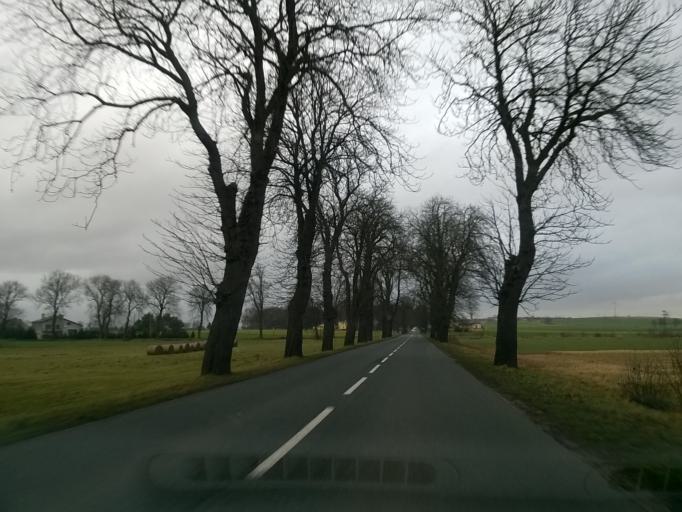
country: PL
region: Kujawsko-Pomorskie
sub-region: Powiat nakielski
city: Kcynia
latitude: 52.9795
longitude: 17.4607
